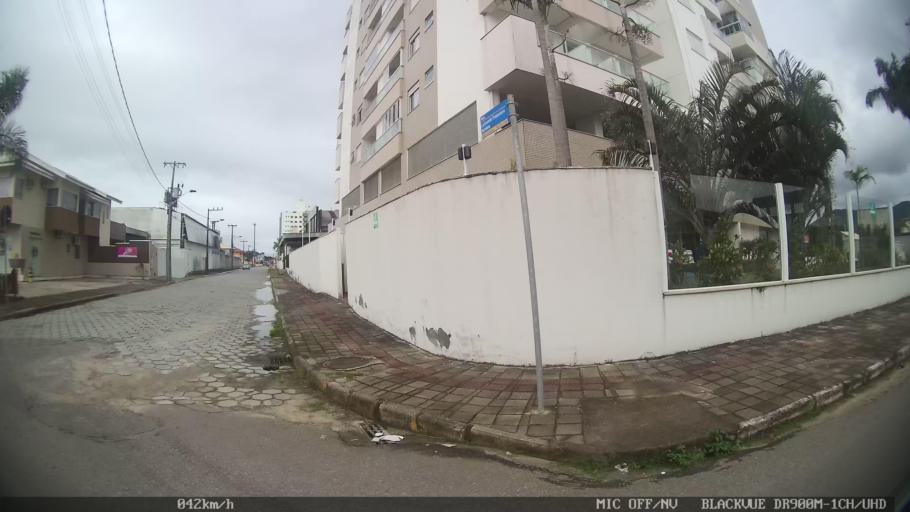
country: BR
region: Santa Catarina
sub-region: Biguacu
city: Biguacu
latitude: -27.5070
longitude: -48.6524
